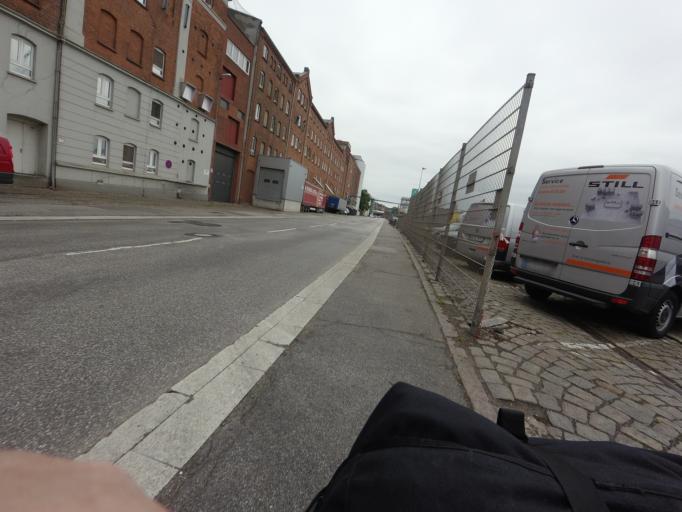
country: DE
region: Schleswig-Holstein
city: Luebeck
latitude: 53.8804
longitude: 10.6914
